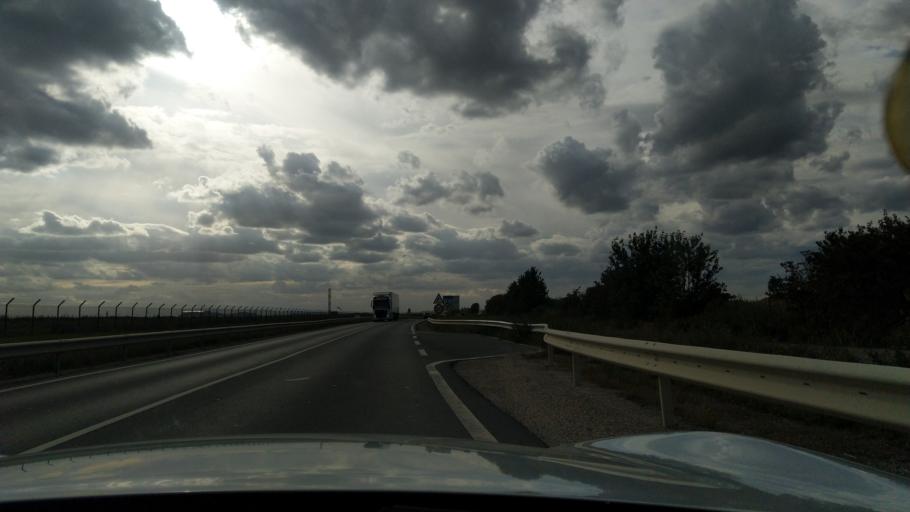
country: FR
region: Ile-de-France
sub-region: Departement du Val-d'Oise
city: Vemars
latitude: 49.0291
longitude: 2.5629
